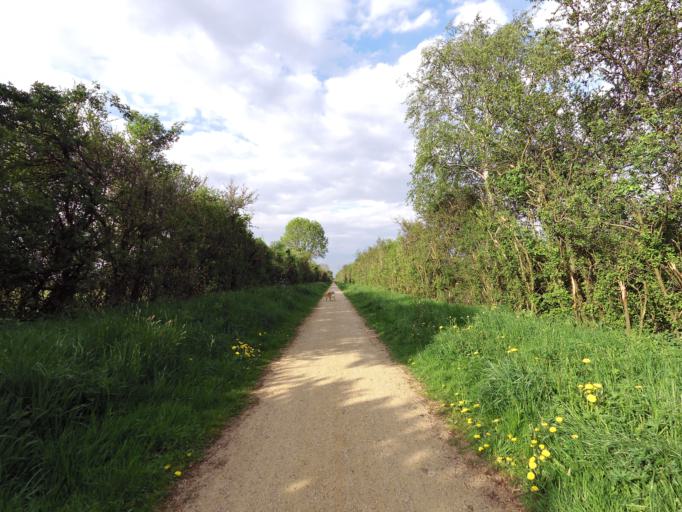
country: DE
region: North Rhine-Westphalia
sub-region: Regierungsbezirk Dusseldorf
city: Kleve
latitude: 51.8100
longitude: 6.1548
